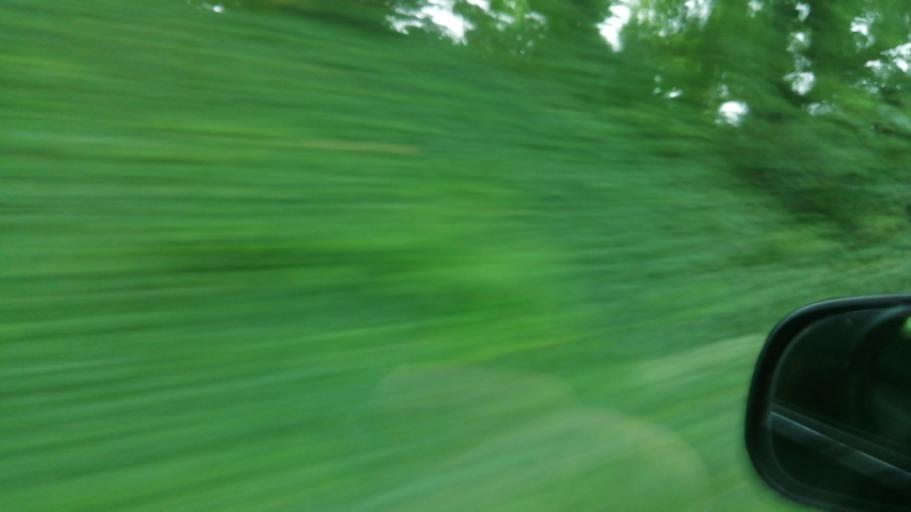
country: IE
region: Munster
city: Fethard
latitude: 52.5401
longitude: -7.6815
